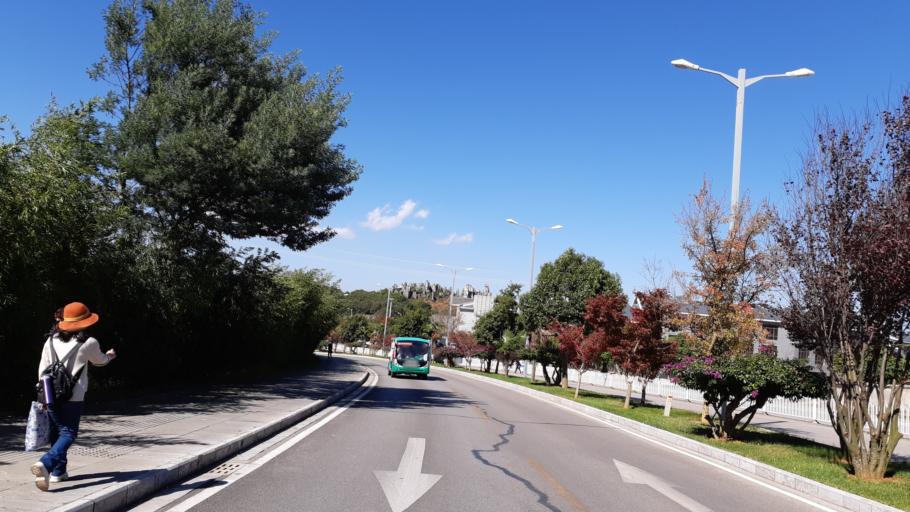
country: CN
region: Yunnan
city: Shilin
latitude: 24.8391
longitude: 103.3312
